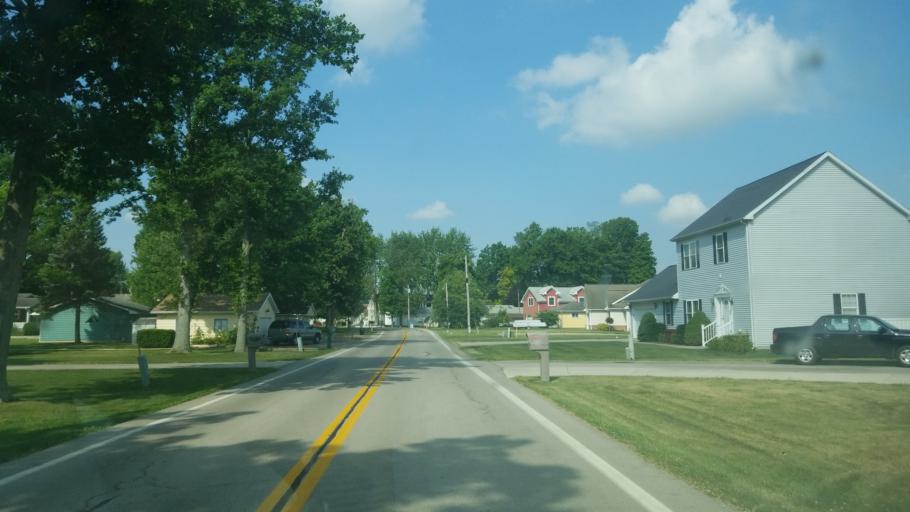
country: US
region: Ohio
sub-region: Logan County
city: Russells Point
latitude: 40.5064
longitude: -83.8478
